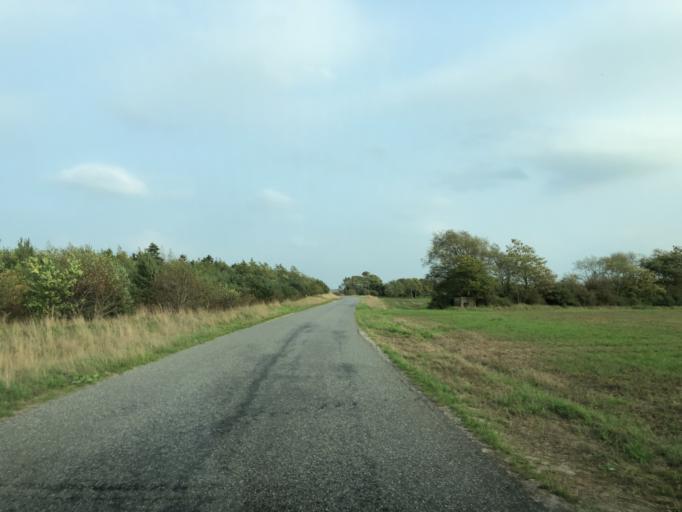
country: DK
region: Central Jutland
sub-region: Ringkobing-Skjern Kommune
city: Videbaek
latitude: 56.1194
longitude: 8.6807
